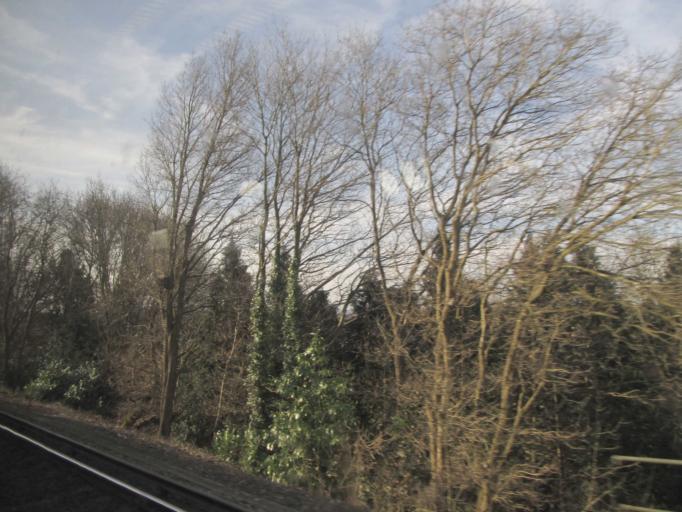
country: GB
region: England
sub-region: Surrey
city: Seale
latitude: 51.2559
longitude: -0.7220
